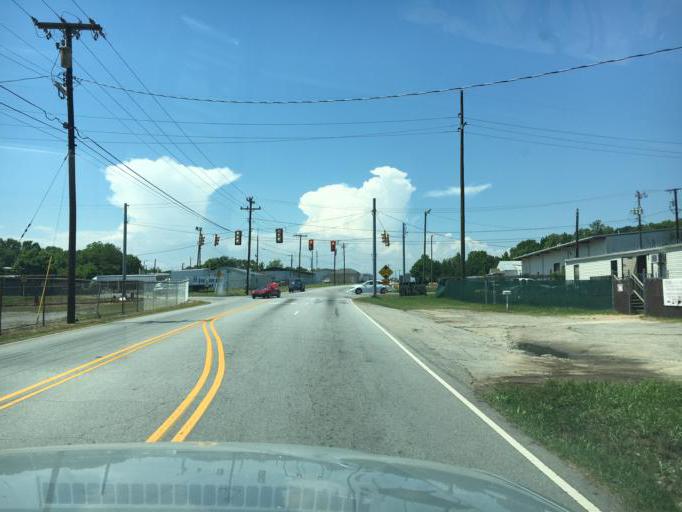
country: US
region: South Carolina
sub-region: Spartanburg County
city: Saxon
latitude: 34.9691
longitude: -81.9633
